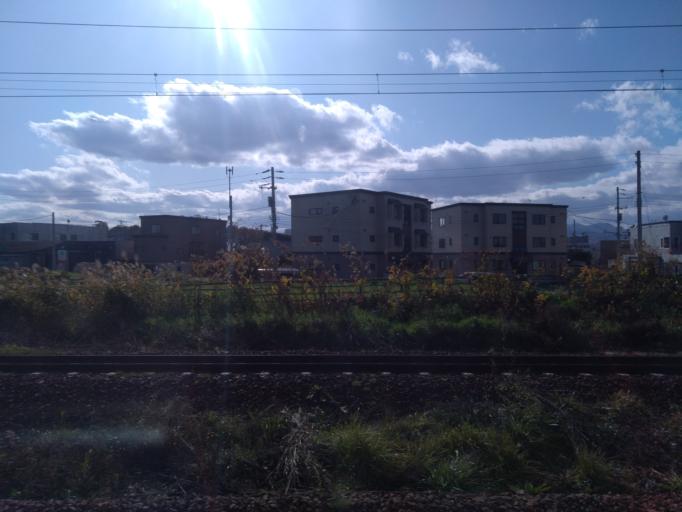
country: JP
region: Hokkaido
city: Sapporo
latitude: 43.0666
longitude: 141.3941
